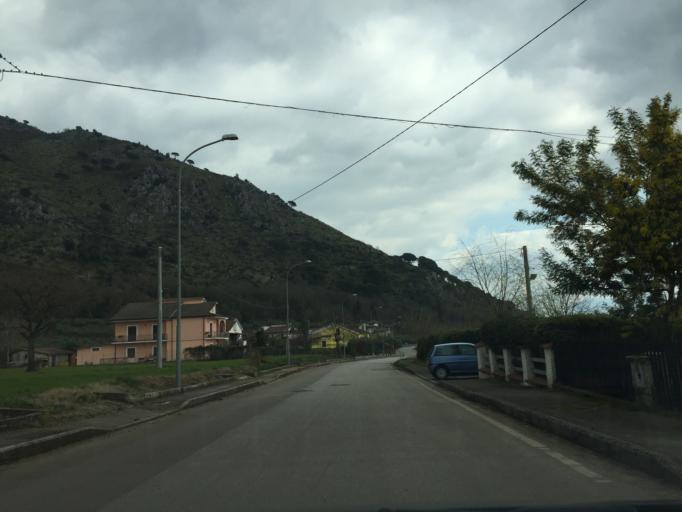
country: IT
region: Latium
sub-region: Provincia di Frosinone
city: Villa Santa Lucia
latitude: 41.4939
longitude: 13.7780
